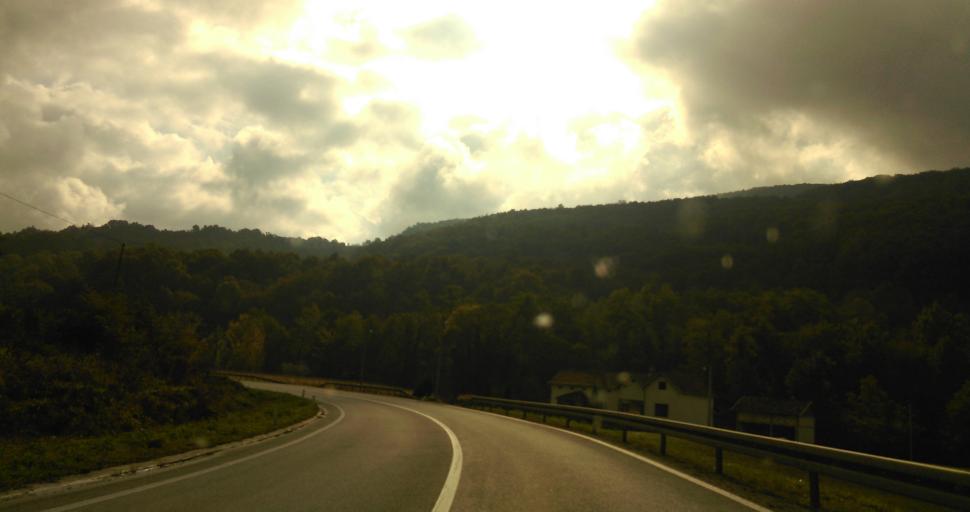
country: RS
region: Central Serbia
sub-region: Kolubarski Okrug
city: Ljig
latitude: 44.1985
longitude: 20.2571
